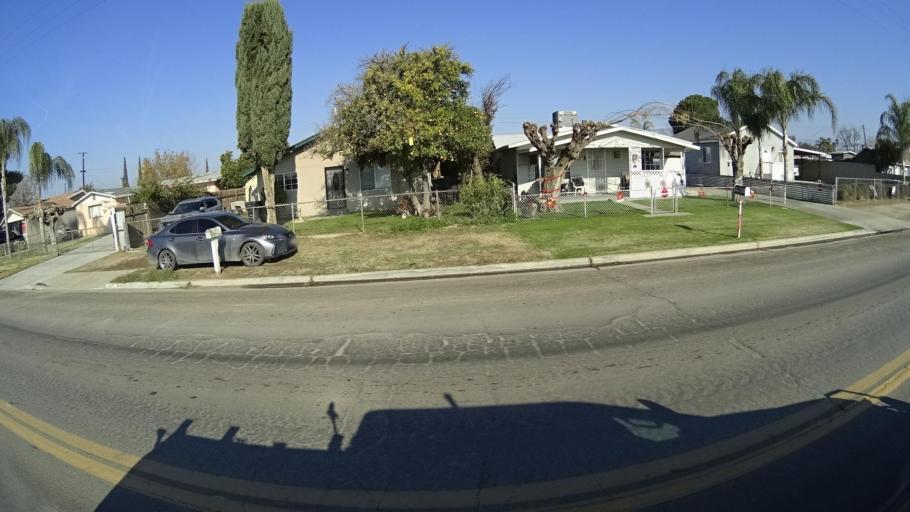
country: US
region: California
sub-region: Kern County
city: Weedpatch
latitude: 35.2378
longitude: -118.9176
